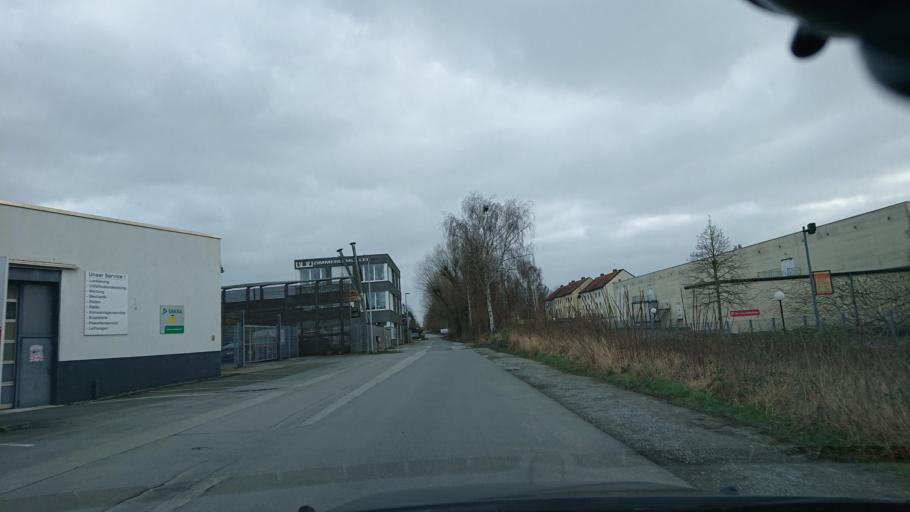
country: DE
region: North Rhine-Westphalia
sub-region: Regierungsbezirk Arnsberg
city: Soest
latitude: 51.5621
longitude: 8.1271
